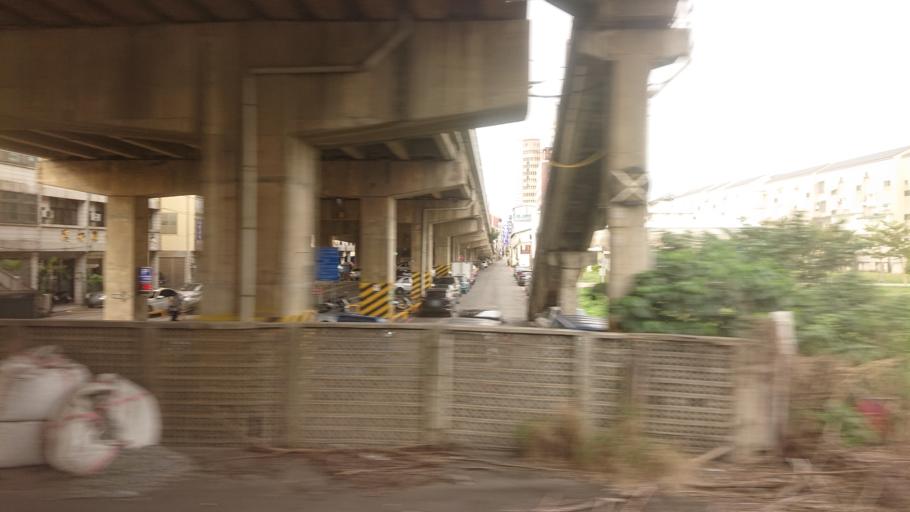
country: TW
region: Taiwan
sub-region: Changhua
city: Chang-hua
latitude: 24.0648
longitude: 120.5321
